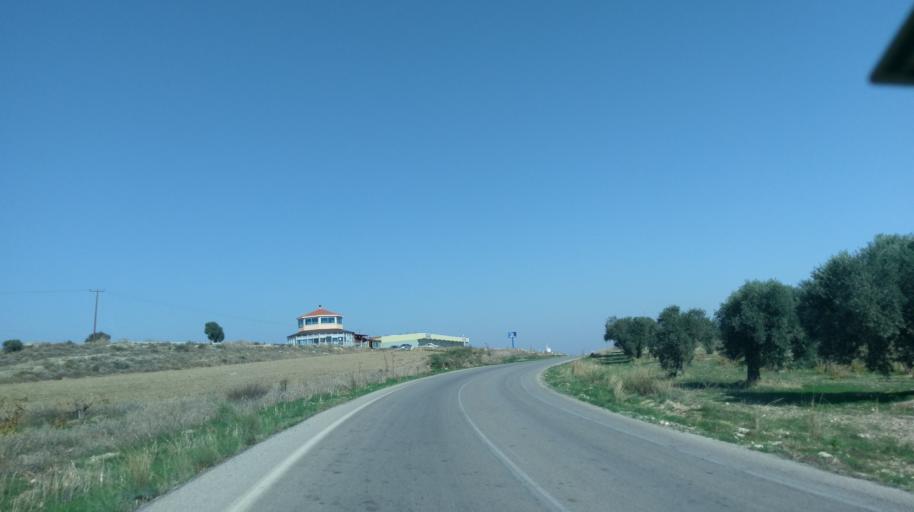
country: CY
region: Ammochostos
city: Leonarisso
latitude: 35.3754
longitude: 34.0357
